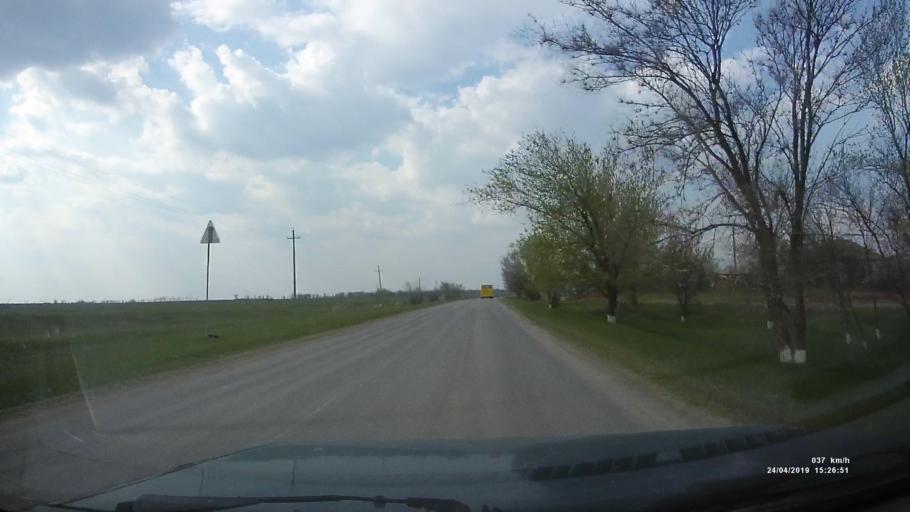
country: RU
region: Rostov
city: Remontnoye
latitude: 46.5596
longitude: 43.0301
